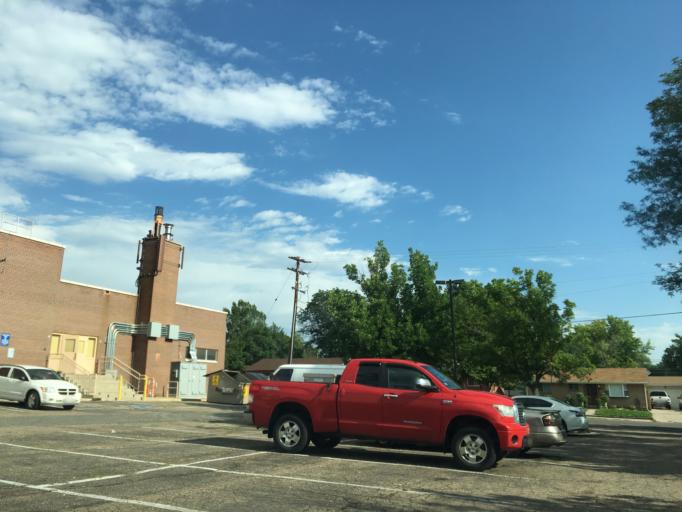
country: US
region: Colorado
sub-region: Arapahoe County
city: Sheridan
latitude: 39.6926
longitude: -105.0333
